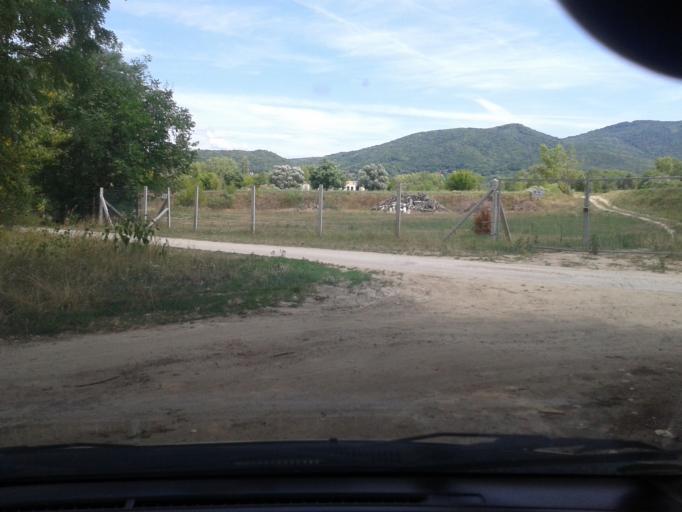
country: HU
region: Komarom-Esztergom
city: Pilismarot
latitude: 47.8009
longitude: 18.8908
